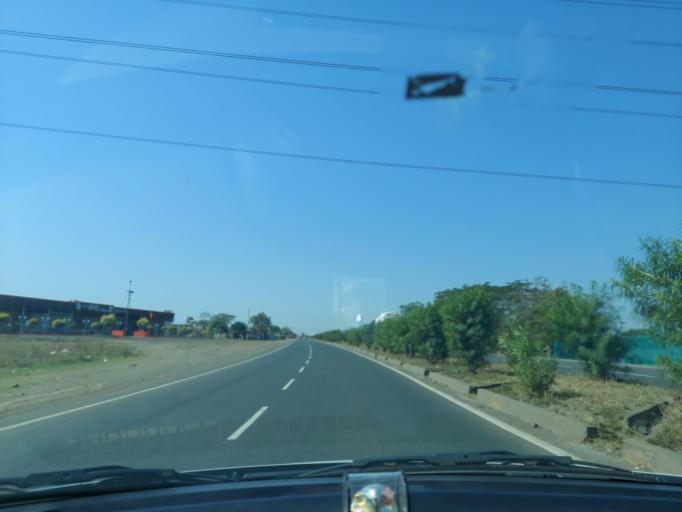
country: IN
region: Madhya Pradesh
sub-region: Indore
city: Manpur
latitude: 22.4220
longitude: 75.6019
